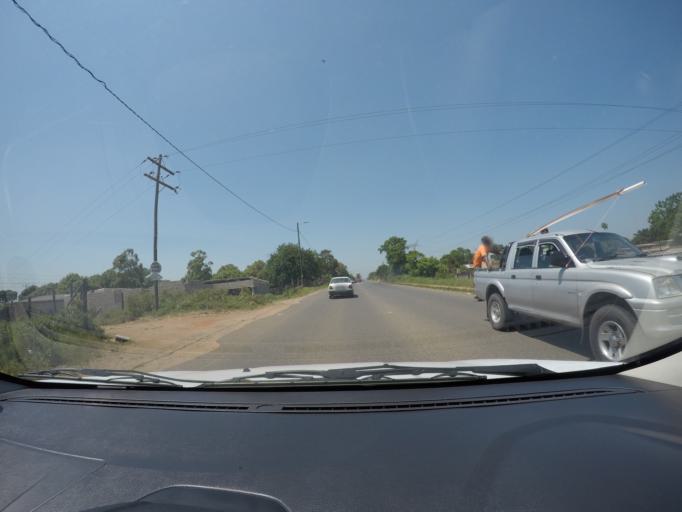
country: ZA
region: KwaZulu-Natal
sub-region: uThungulu District Municipality
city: eSikhawini
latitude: -28.8265
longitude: 31.9441
